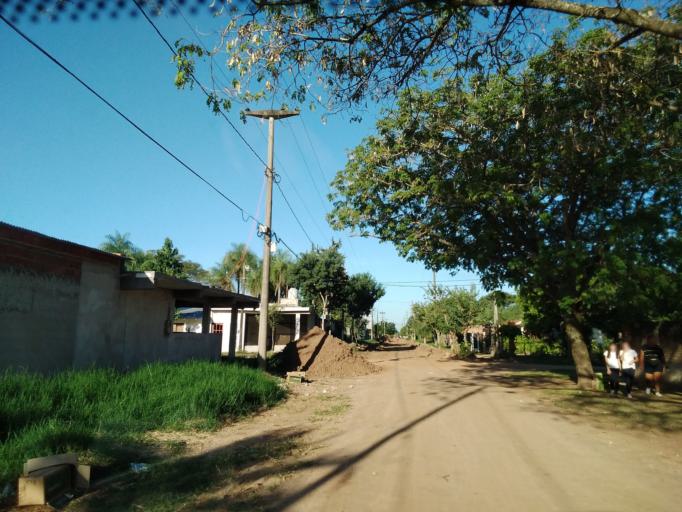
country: AR
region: Corrientes
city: Corrientes
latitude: -27.5060
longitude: -58.7960
